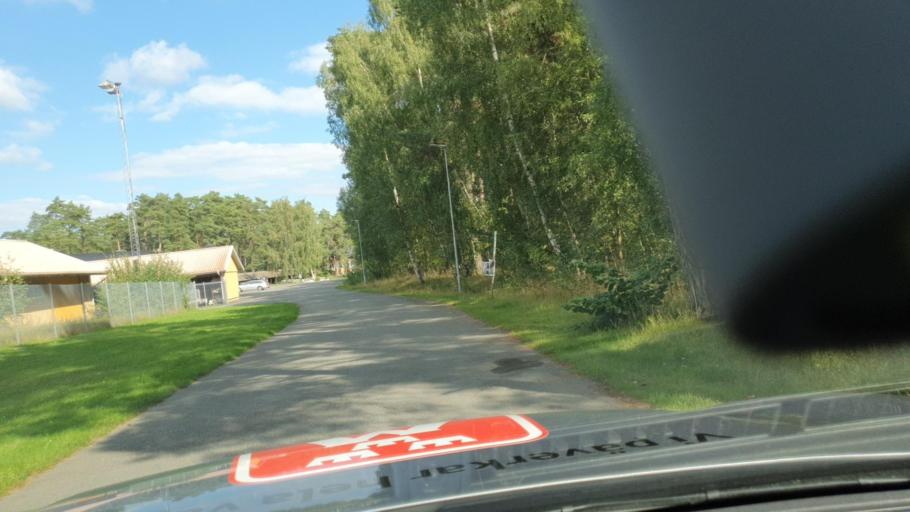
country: SE
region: Skane
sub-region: Kristianstads Kommun
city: Norra Asum
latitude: 55.9864
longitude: 14.1362
